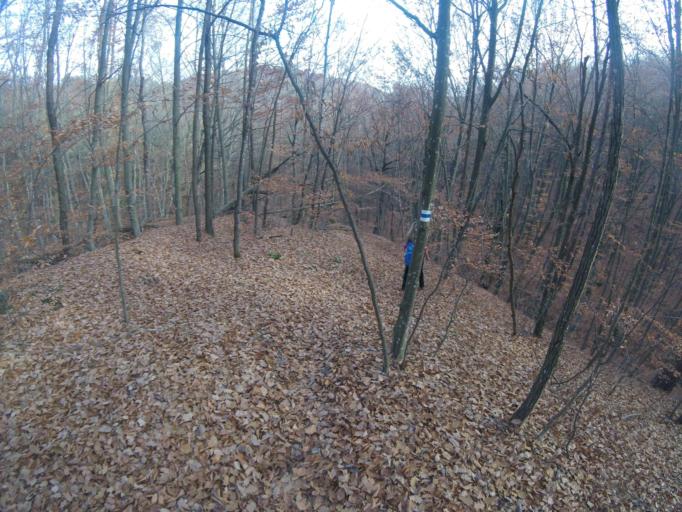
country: HU
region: Borsod-Abauj-Zemplen
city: Sarospatak
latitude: 48.4303
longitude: 21.5055
